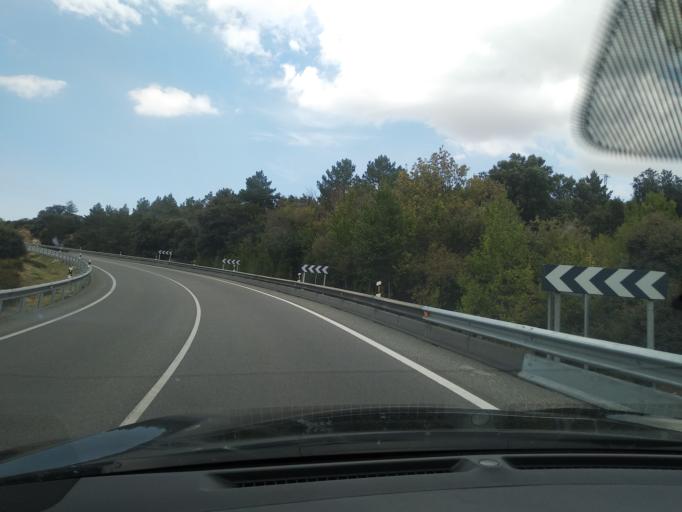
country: ES
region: Castille and Leon
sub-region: Provincia de Segovia
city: Palazuelos de Eresma
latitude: 40.8641
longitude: -4.0978
